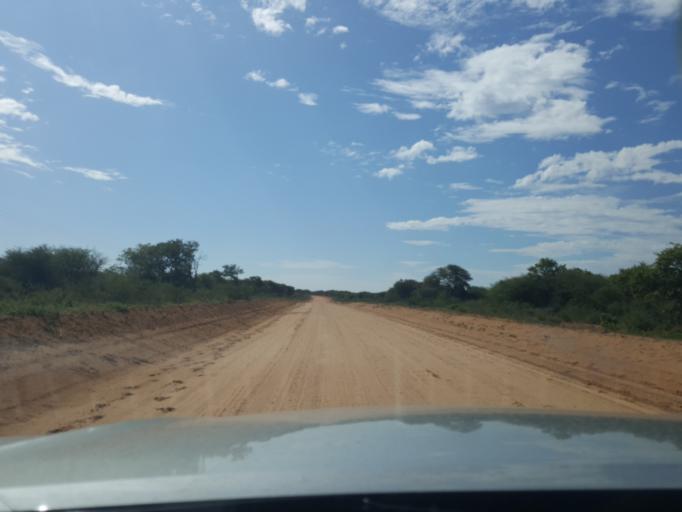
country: BW
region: Kweneng
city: Khudumelapye
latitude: -23.8117
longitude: 24.8202
